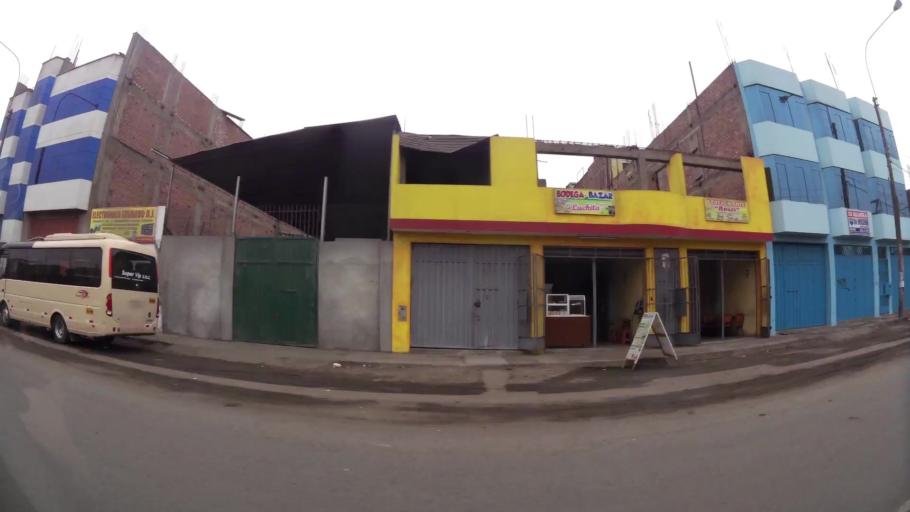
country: PE
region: Lima
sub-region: Lima
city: Vitarte
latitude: -12.0384
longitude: -76.9555
